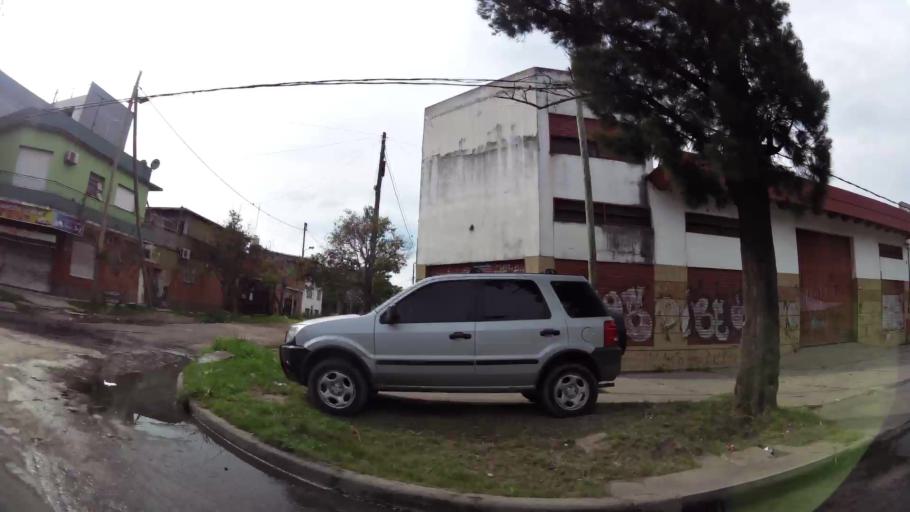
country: AR
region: Buenos Aires
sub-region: Partido de Quilmes
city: Quilmes
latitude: -34.7078
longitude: -58.2321
